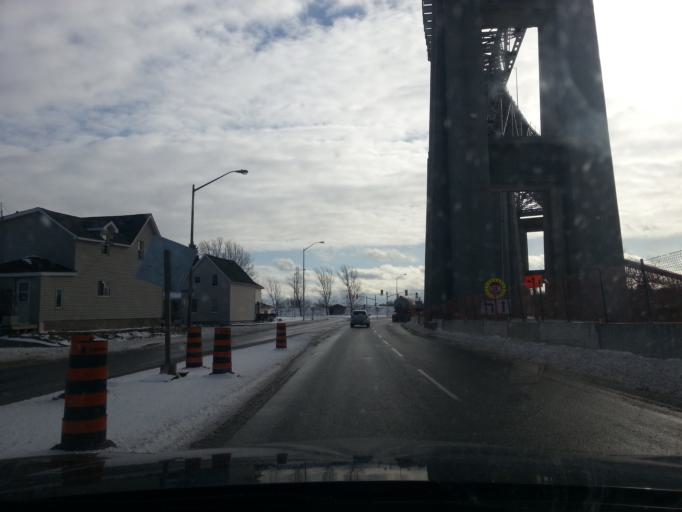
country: CA
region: Ontario
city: Cornwall
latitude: 45.0133
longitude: -74.7398
